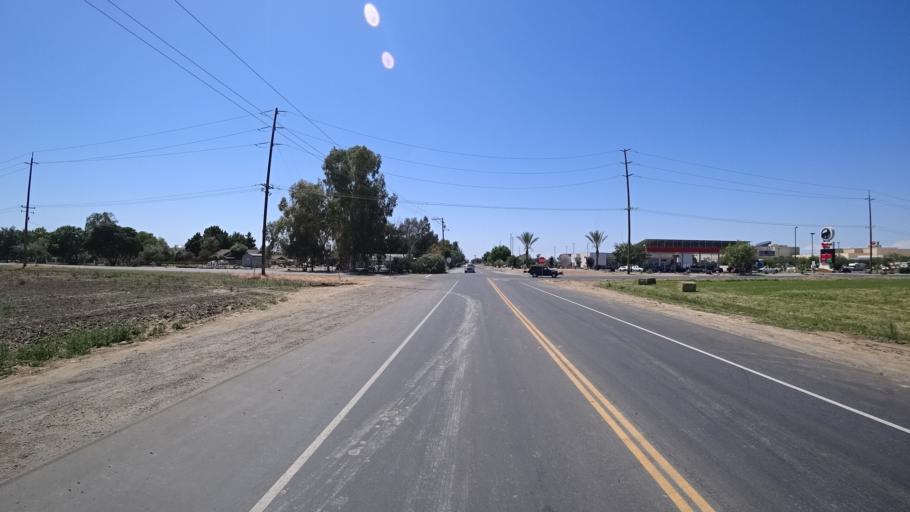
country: US
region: California
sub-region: Kings County
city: Lemoore
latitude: 36.2405
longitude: -119.7628
